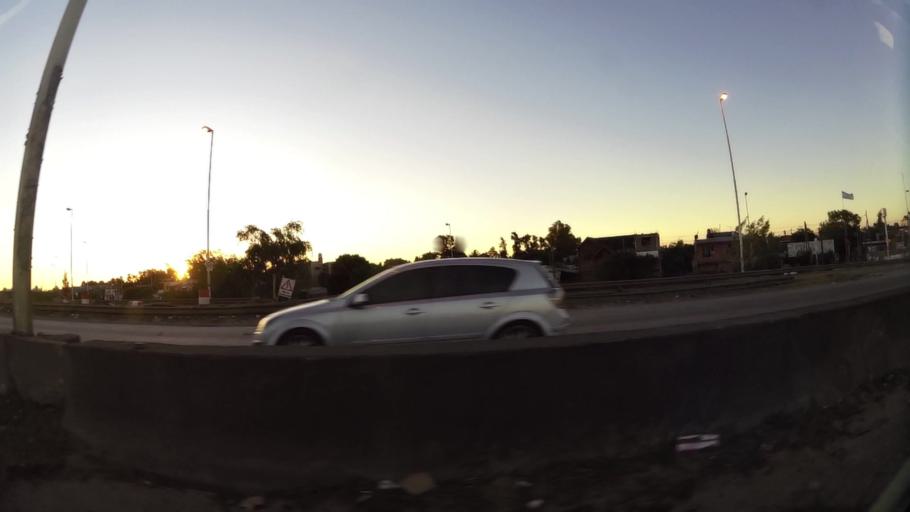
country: AR
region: Buenos Aires
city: Pontevedra
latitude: -34.7575
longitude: -58.6152
